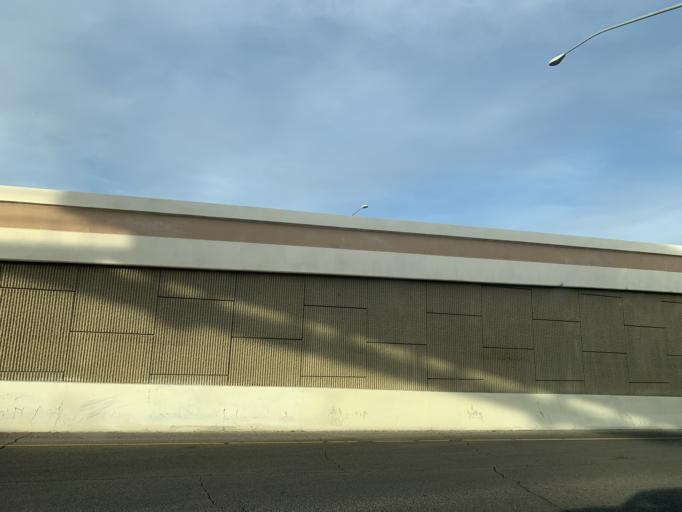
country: US
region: Nevada
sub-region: Clark County
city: Paradise
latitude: 36.1295
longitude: -115.1830
